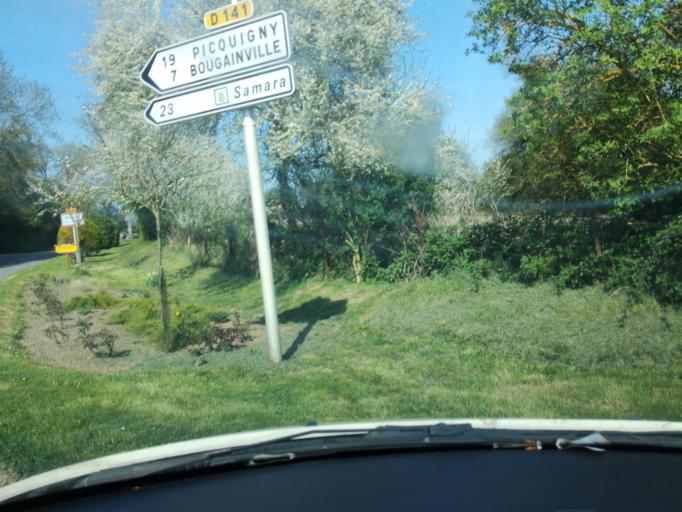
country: FR
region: Picardie
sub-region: Departement de la Somme
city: Poix-de-Picardie
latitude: 49.8182
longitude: 2.0173
